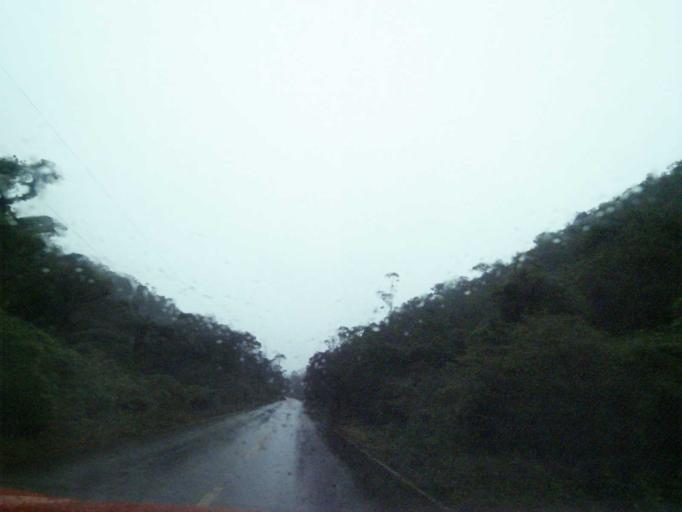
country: BR
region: Santa Catarina
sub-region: Anitapolis
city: Anitapolis
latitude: -27.7741
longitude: -49.0411
